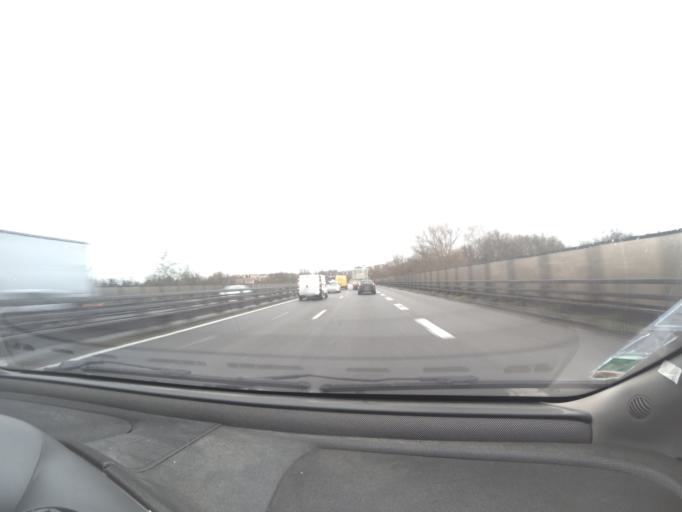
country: FR
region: Pays de la Loire
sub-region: Departement de la Loire-Atlantique
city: Saint-Sebastien-sur-Loire
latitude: 47.1754
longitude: -1.5098
